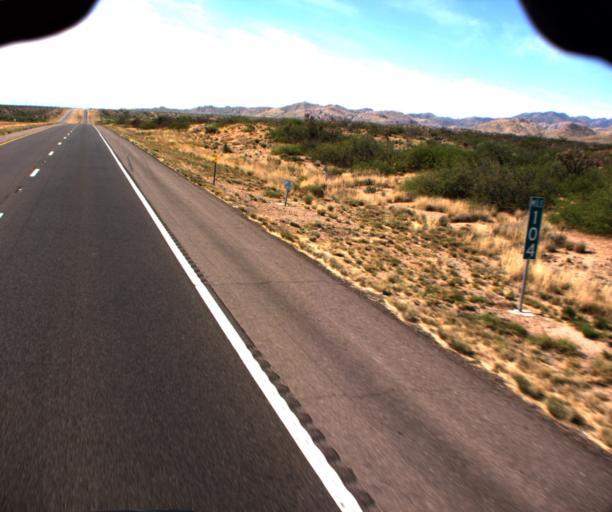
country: US
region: Arizona
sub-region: Graham County
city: Swift Trail Junction
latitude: 32.5925
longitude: -109.6845
